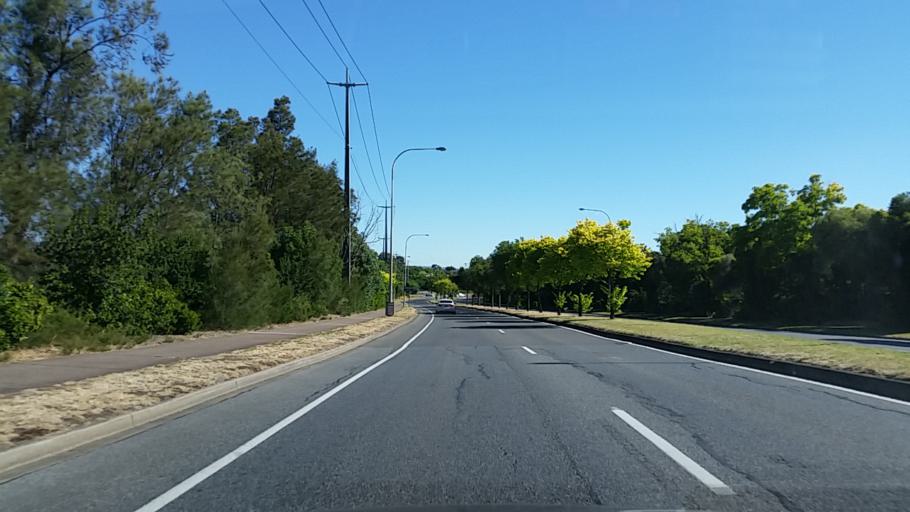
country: AU
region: South Australia
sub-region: Tea Tree Gully
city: Modbury
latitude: -34.8006
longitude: 138.6853
